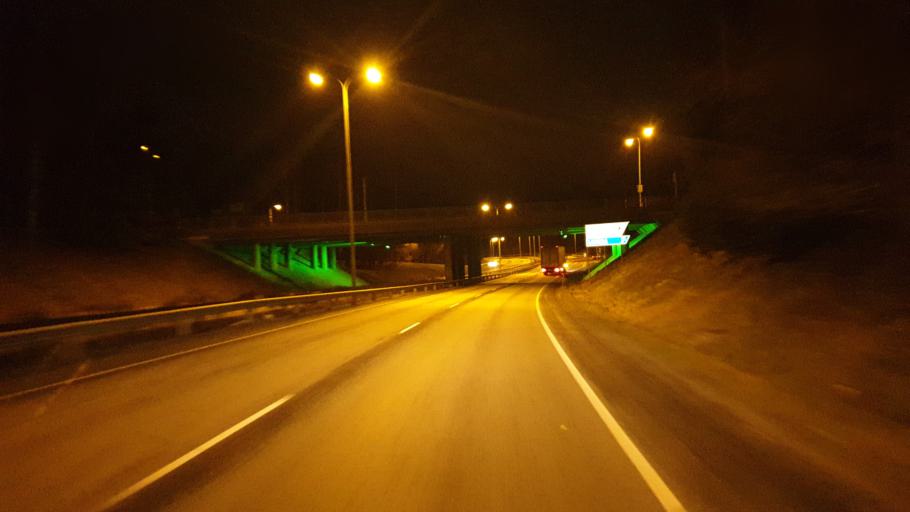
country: FI
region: Central Finland
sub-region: Jyvaeskylae
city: Jyvaeskylae
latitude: 62.2567
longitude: 25.7580
